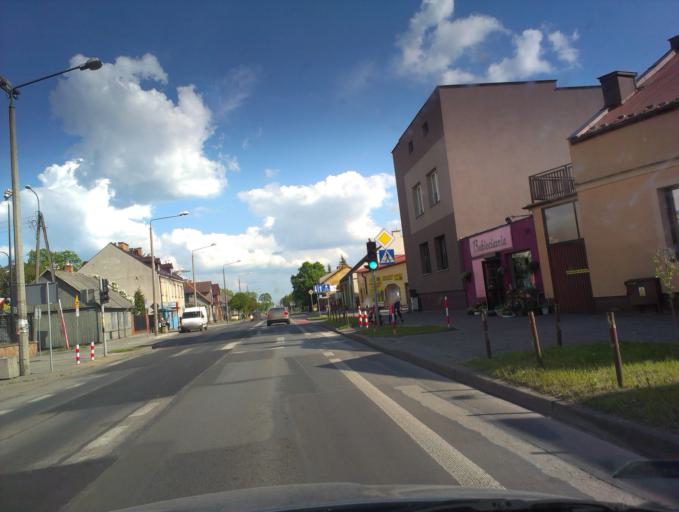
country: PL
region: Masovian Voivodeship
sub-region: Radom
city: Radom
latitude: 51.3873
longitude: 21.1747
